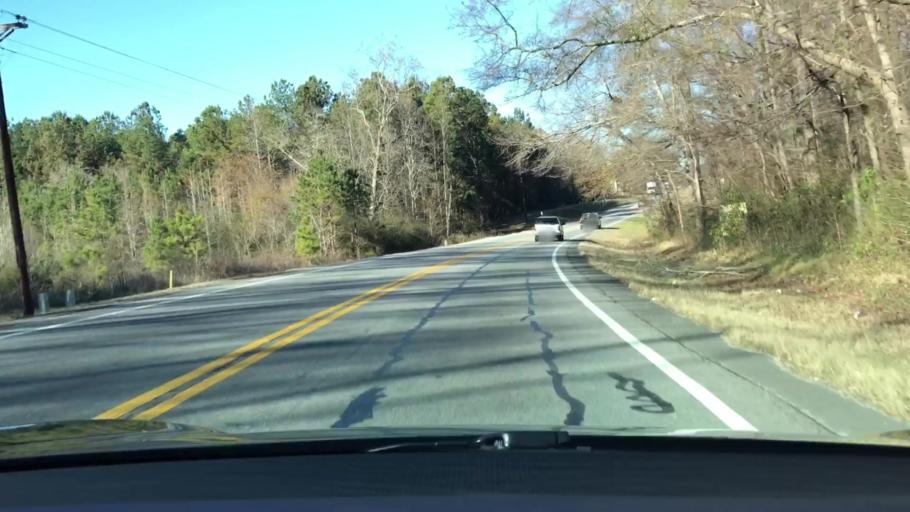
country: US
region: Georgia
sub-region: Walton County
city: Monroe
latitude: 33.8756
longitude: -83.7210
